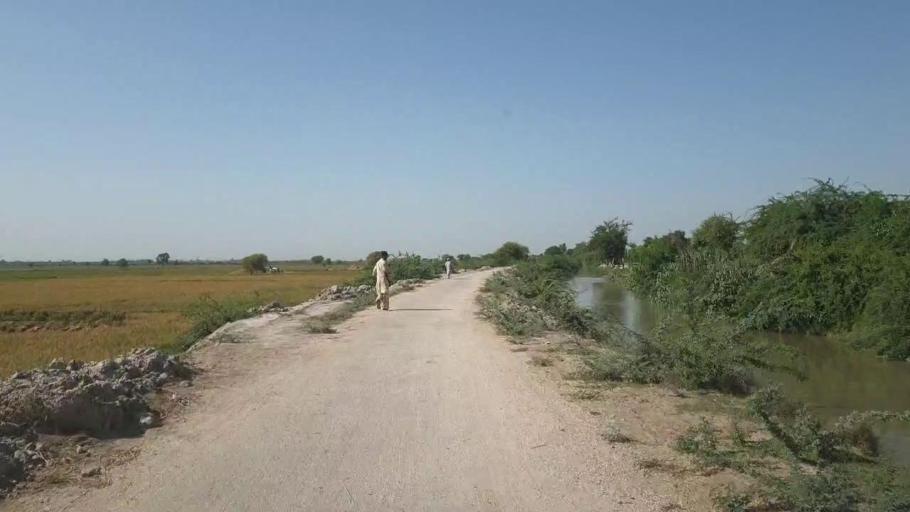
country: PK
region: Sindh
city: Kadhan
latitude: 24.5734
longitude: 68.9863
